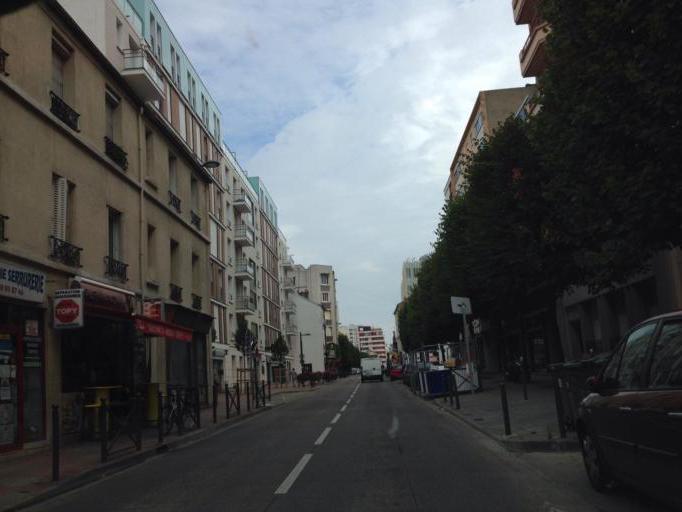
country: FR
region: Ile-de-France
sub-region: Departement des Hauts-de-Seine
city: Vanves
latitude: 48.8213
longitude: 2.2926
